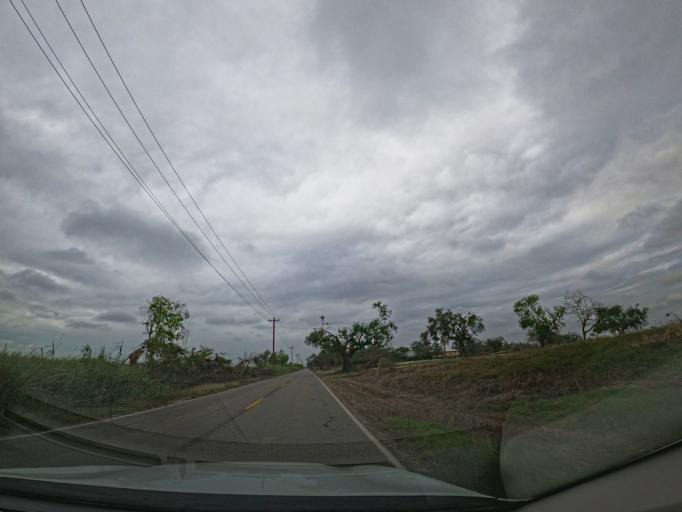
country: US
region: Louisiana
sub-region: Cameron Parish
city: Cameron
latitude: 29.7590
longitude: -92.9364
